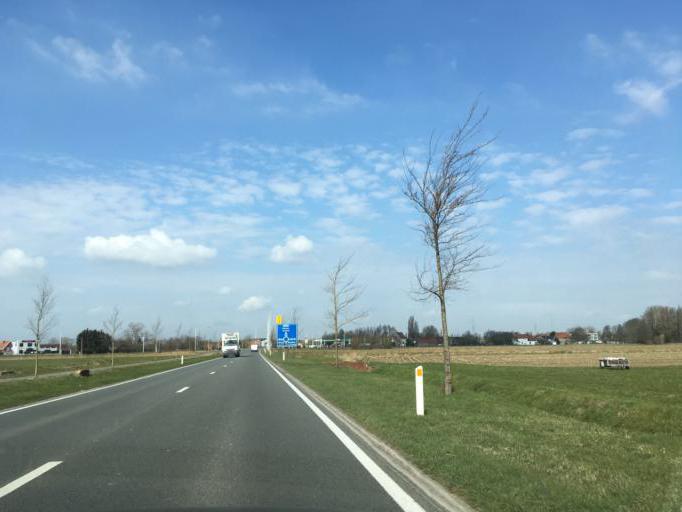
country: BE
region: Flanders
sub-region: Provincie West-Vlaanderen
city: Kuurne
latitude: 50.8747
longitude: 3.2763
